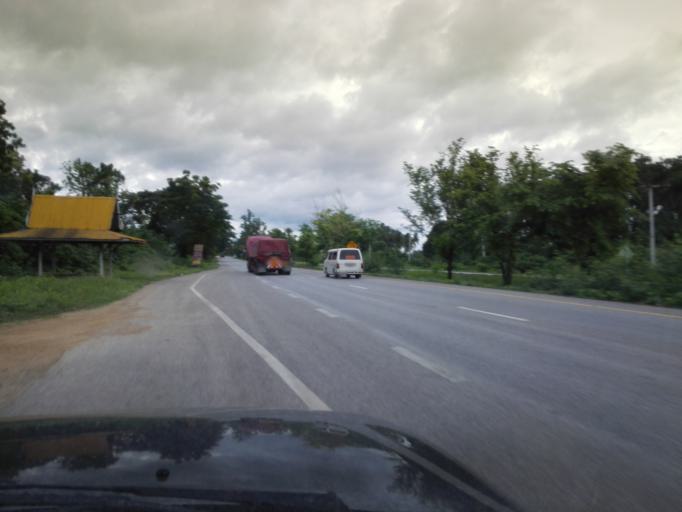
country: TH
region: Tak
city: Tak
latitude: 16.7909
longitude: 99.1638
